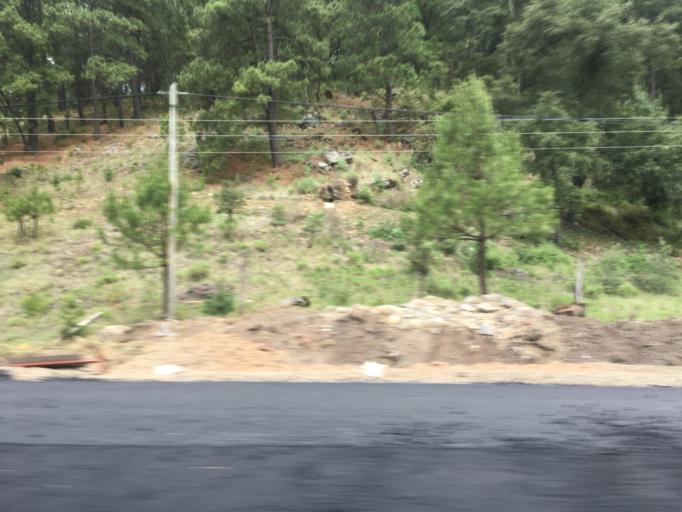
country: MX
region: Mexico
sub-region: Morelos
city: San Marcos Tlazalpan
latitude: 19.8445
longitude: -99.7028
